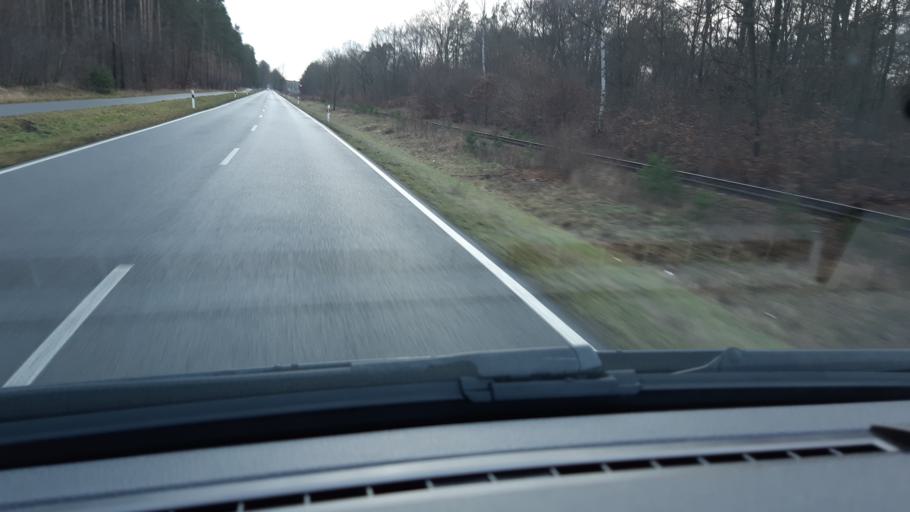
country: DE
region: Brandenburg
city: Zehdenick
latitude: 53.0460
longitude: 13.3919
